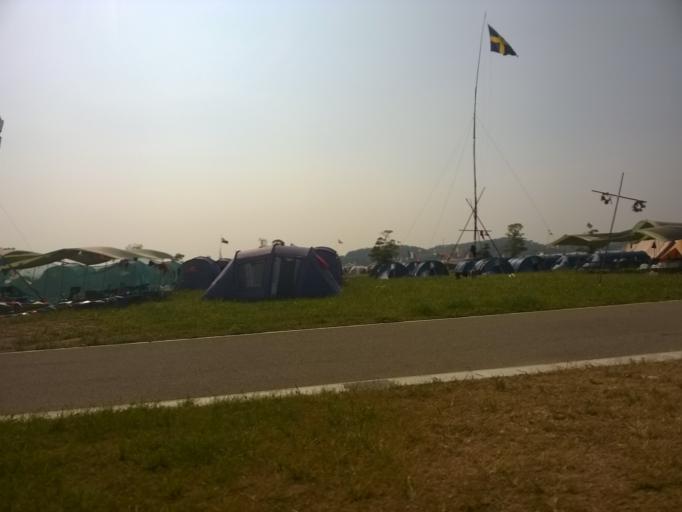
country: JP
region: Yamaguchi
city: Ogori-shimogo
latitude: 34.0125
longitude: 131.3753
